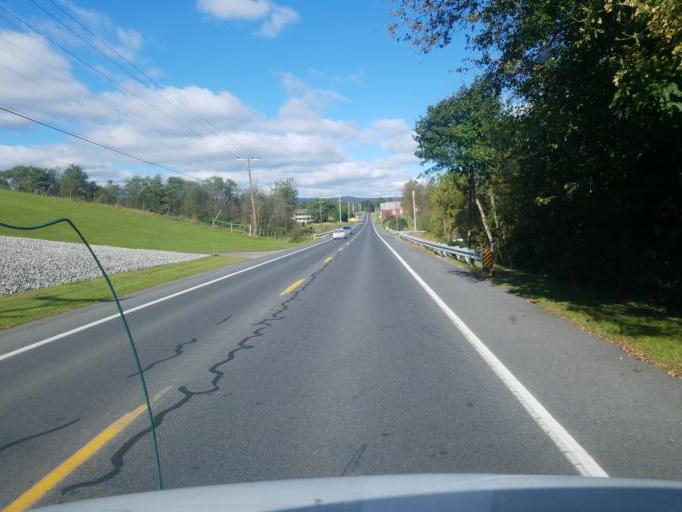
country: US
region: Pennsylvania
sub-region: Franklin County
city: Mercersburg
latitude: 39.8155
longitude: -77.8898
